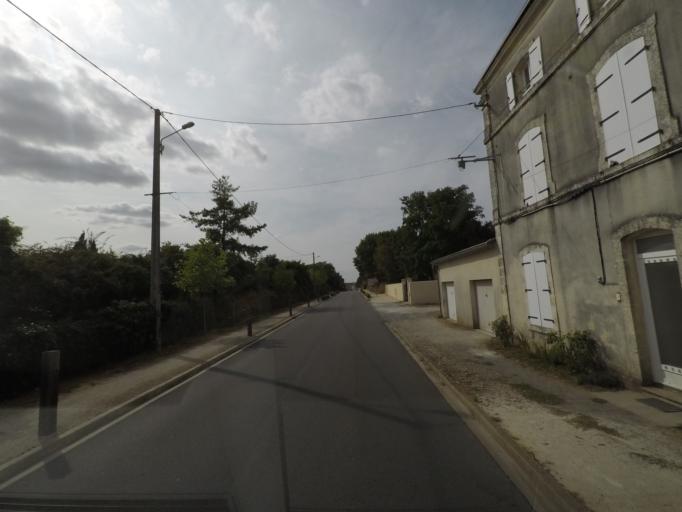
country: FR
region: Poitou-Charentes
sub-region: Departement de la Charente
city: Ruffec
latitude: 46.0268
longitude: 0.2124
